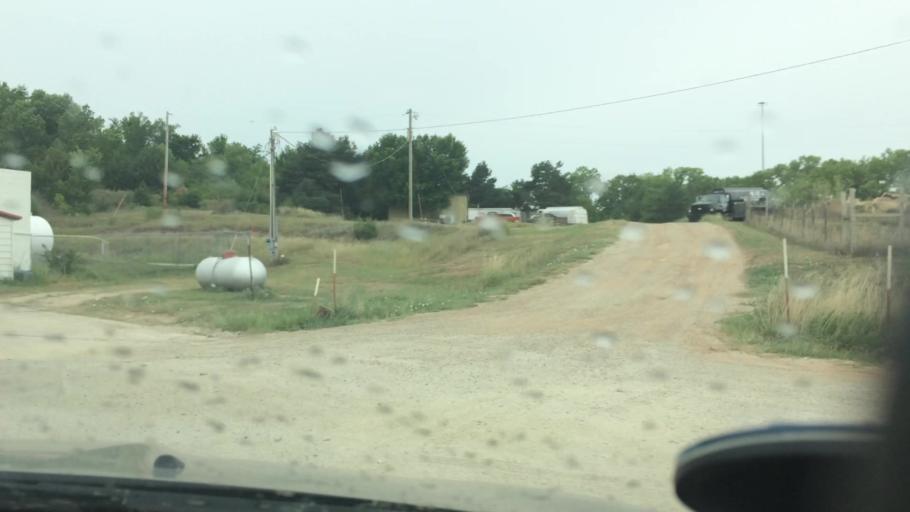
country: US
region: Kansas
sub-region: Ellsworth County
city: Ellsworth
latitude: 38.8572
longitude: -98.1115
